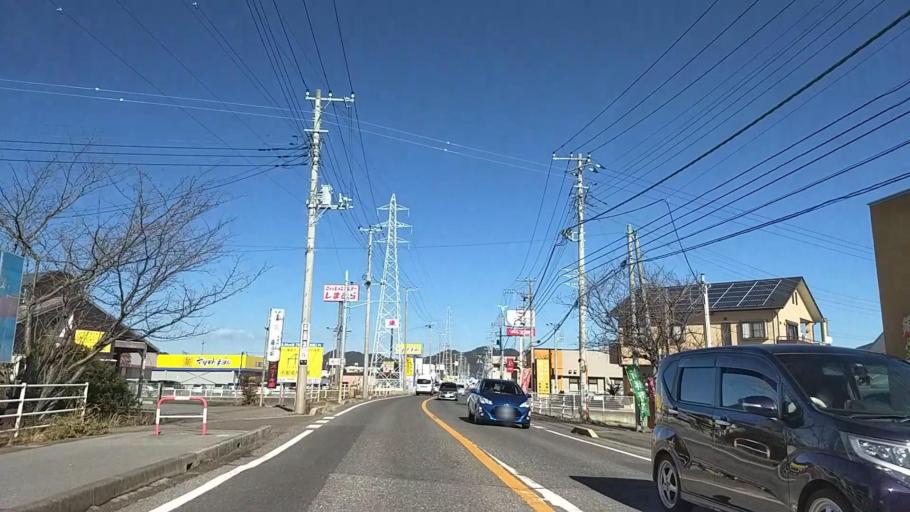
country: JP
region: Chiba
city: Kawaguchi
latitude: 35.1012
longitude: 140.0943
